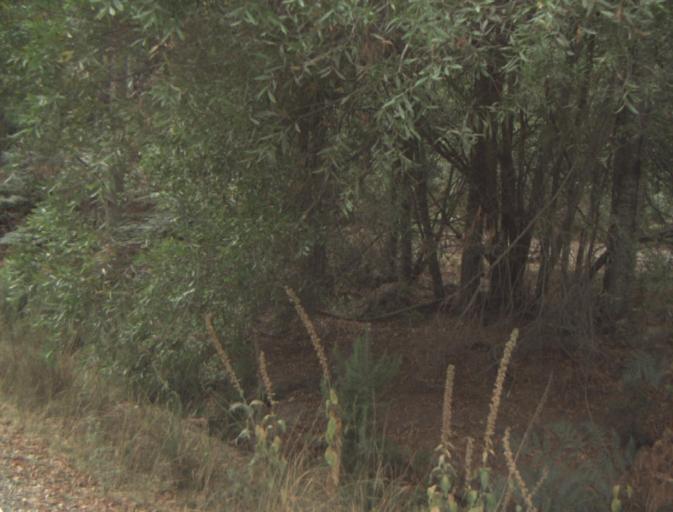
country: AU
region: Tasmania
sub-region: Launceston
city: Mayfield
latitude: -41.1574
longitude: 147.1734
